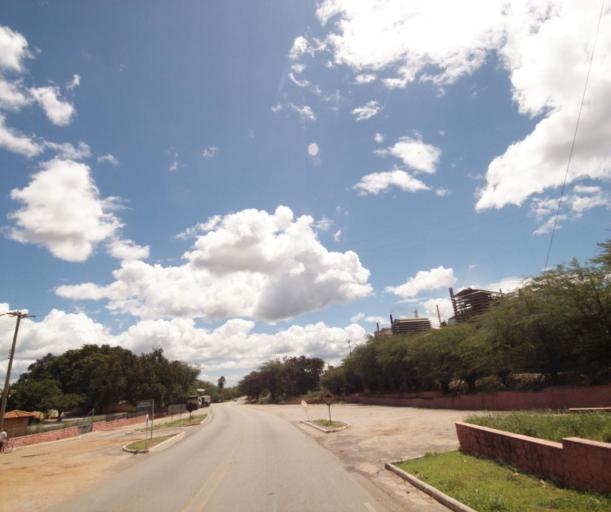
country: BR
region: Bahia
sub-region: Brumado
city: Brumado
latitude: -14.2400
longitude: -41.7236
